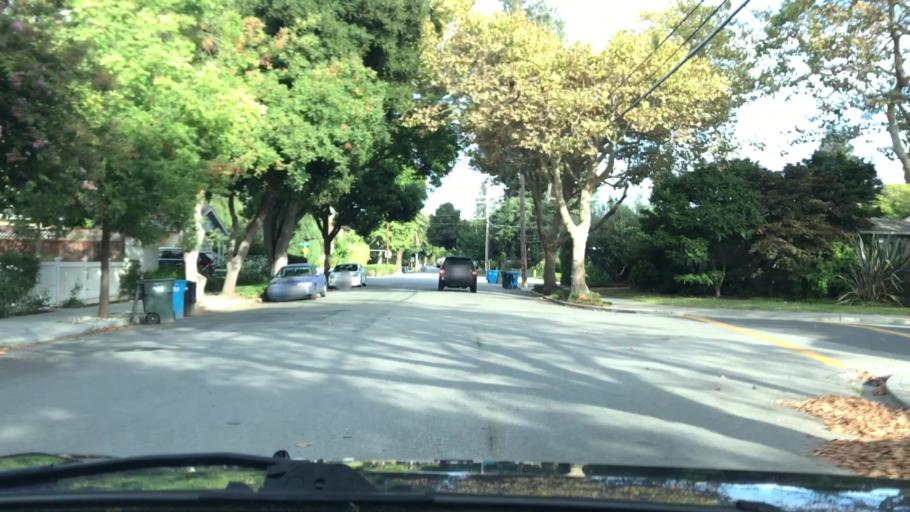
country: US
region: California
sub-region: San Mateo County
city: East Palo Alto
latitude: 37.4598
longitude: -122.1588
